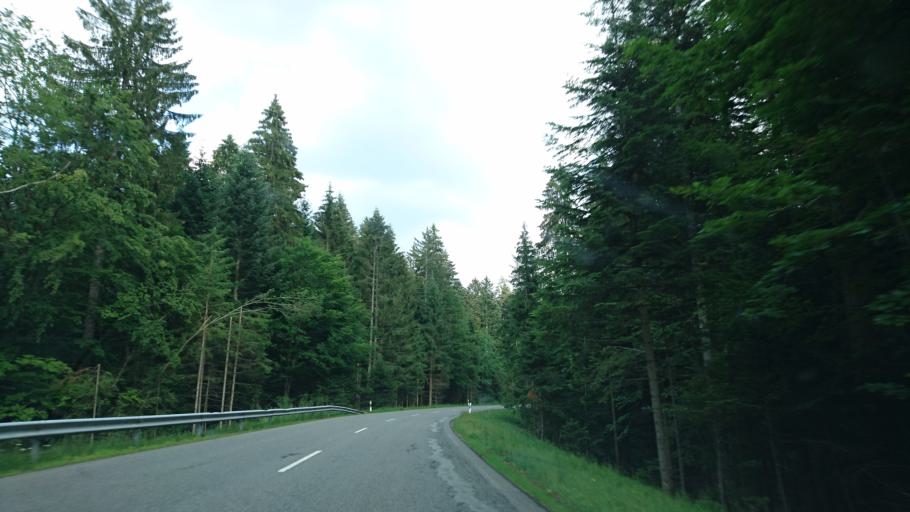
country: DE
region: Bavaria
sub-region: Lower Bavaria
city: Neuschonau
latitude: 48.9134
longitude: 13.4632
